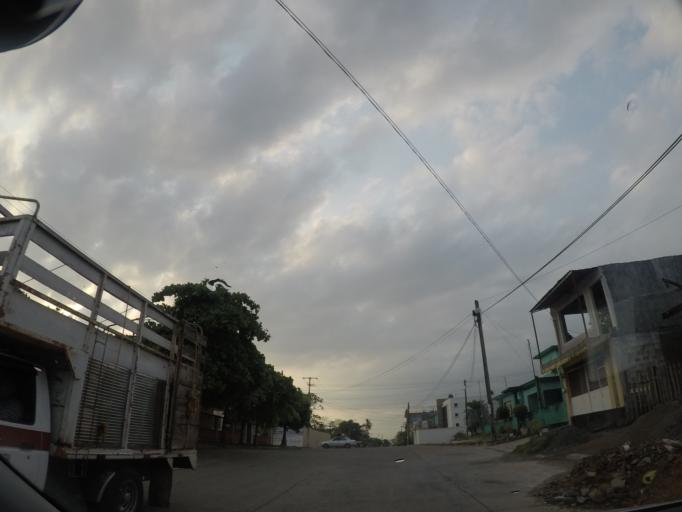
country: MX
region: Oaxaca
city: Matias Romero
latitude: 16.8732
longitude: -95.0382
